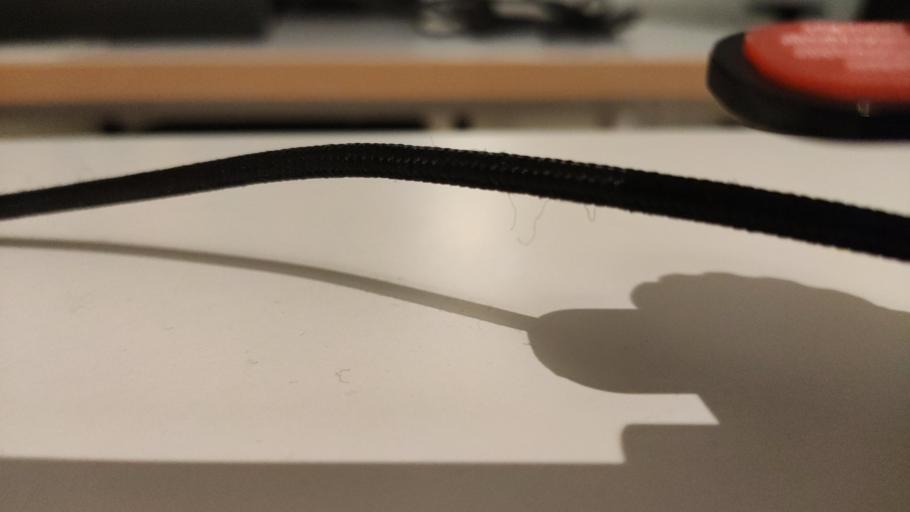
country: RU
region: Moskovskaya
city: Gorshkovo
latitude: 56.3723
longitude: 37.3757
